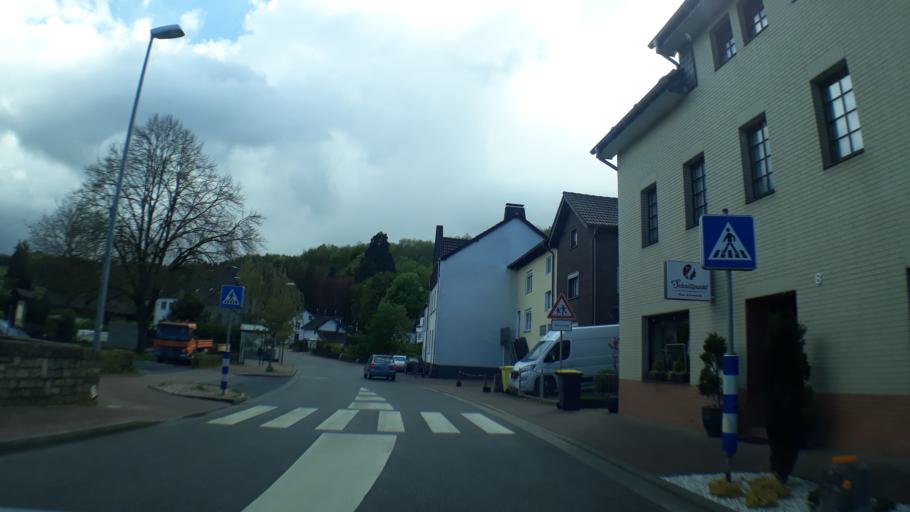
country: DE
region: North Rhine-Westphalia
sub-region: Regierungsbezirk Koln
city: Kall
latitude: 50.5248
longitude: 6.5561
